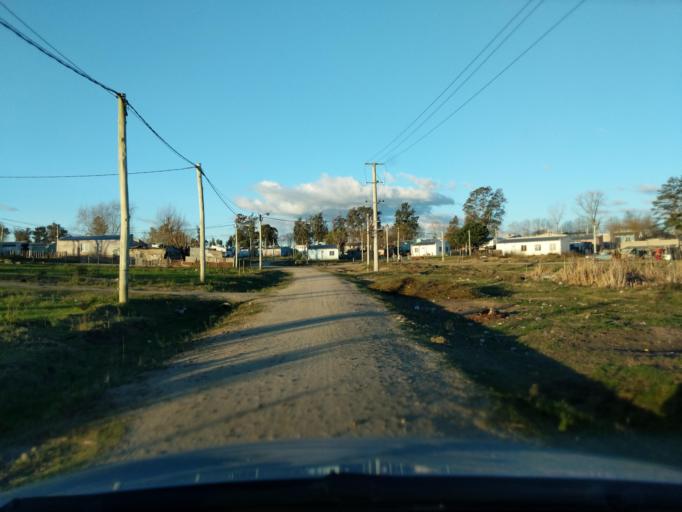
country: UY
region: Florida
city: Florida
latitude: -34.1038
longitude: -56.2384
